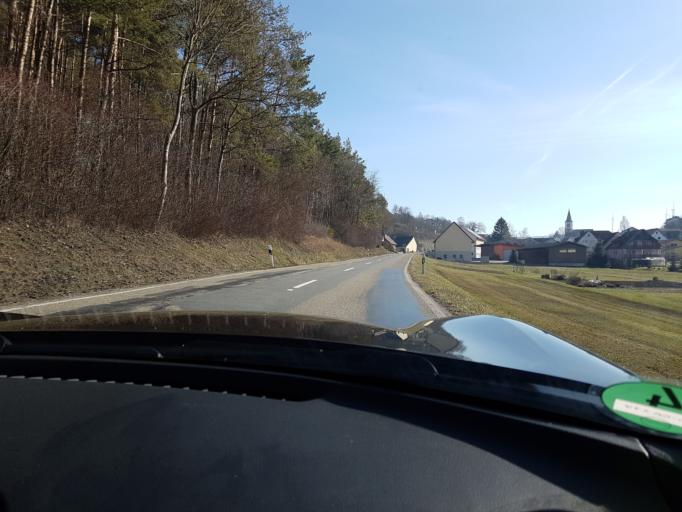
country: DE
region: Baden-Wuerttemberg
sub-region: Regierungsbezirk Stuttgart
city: Dorzbach
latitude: 49.3665
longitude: 9.6744
